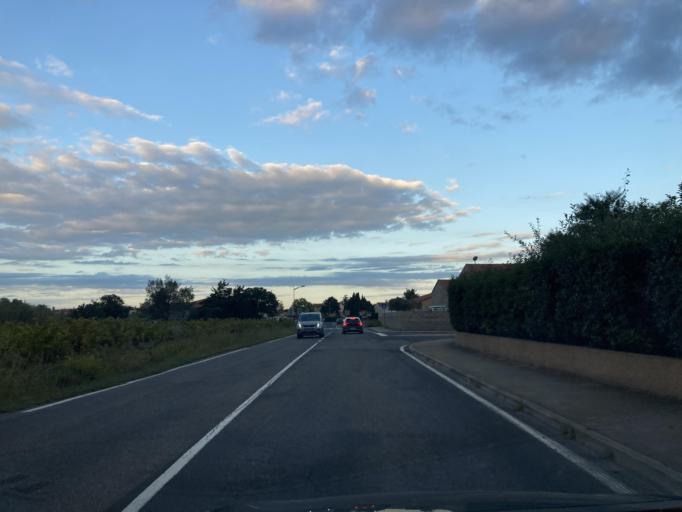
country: FR
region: Languedoc-Roussillon
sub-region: Departement des Pyrenees-Orientales
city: Sant Genis de Fontanes
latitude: 42.5641
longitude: 2.8982
